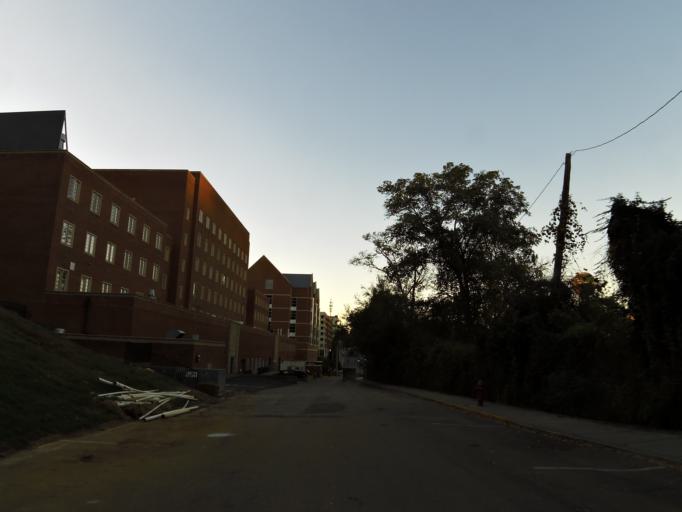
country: US
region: Tennessee
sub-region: Knox County
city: Knoxville
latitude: 35.9572
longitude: -83.9233
